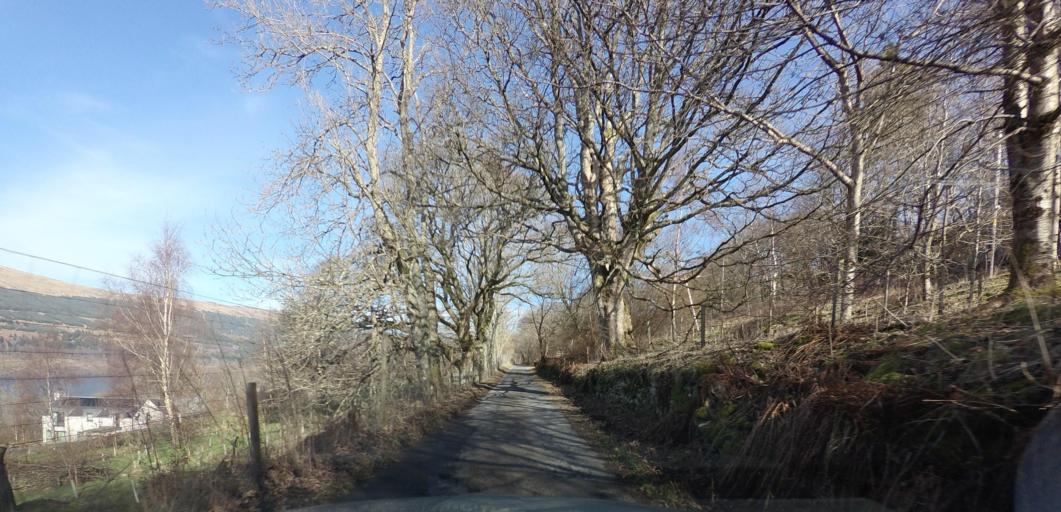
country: GB
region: Scotland
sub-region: Perth and Kinross
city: Comrie
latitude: 56.5416
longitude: -4.1014
